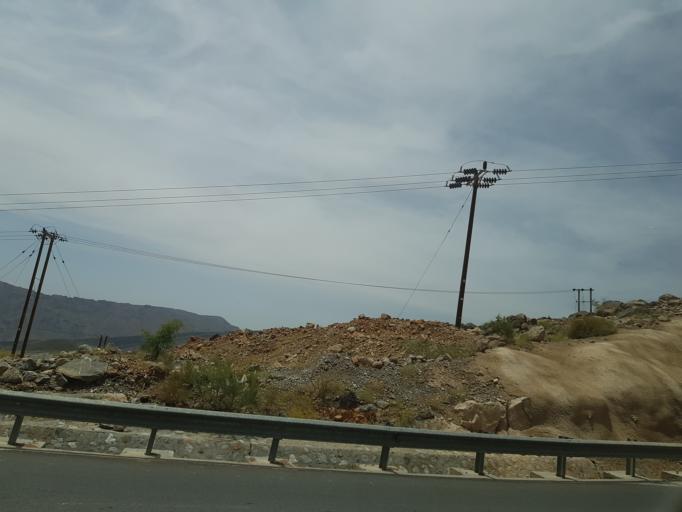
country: OM
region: Muhafazat ad Dakhiliyah
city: Izki
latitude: 22.9819
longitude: 57.7009
